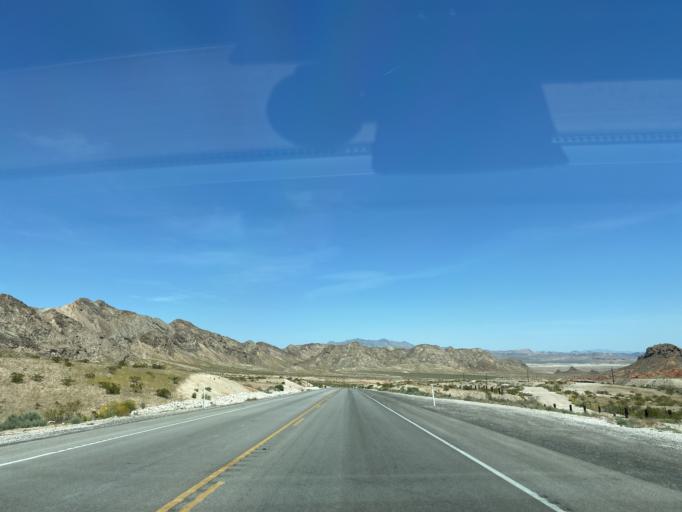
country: US
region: Nevada
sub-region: Clark County
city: Nellis Air Force Base
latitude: 36.2035
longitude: -114.9715
